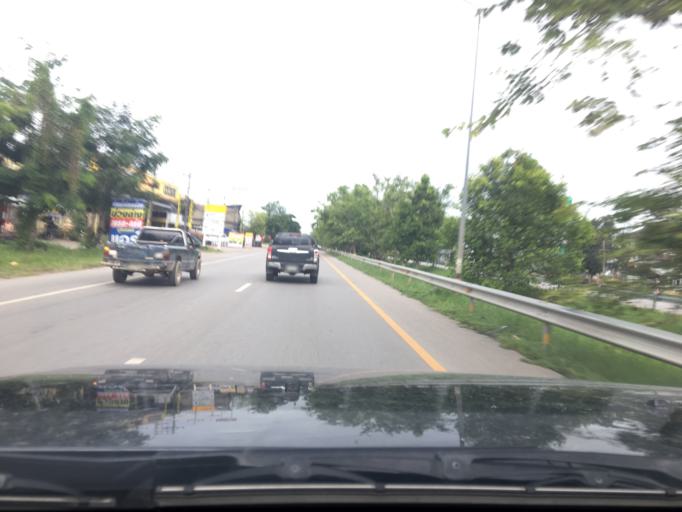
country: TH
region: Chiang Rai
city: Chiang Rai
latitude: 19.8543
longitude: 99.8140
